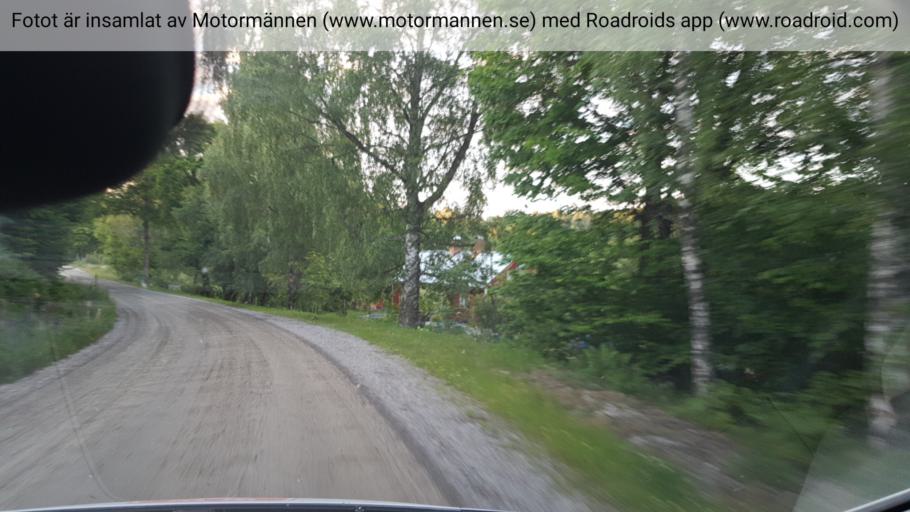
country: SE
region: Vaermland
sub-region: Sunne Kommun
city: Sunne
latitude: 59.7002
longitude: 12.8852
